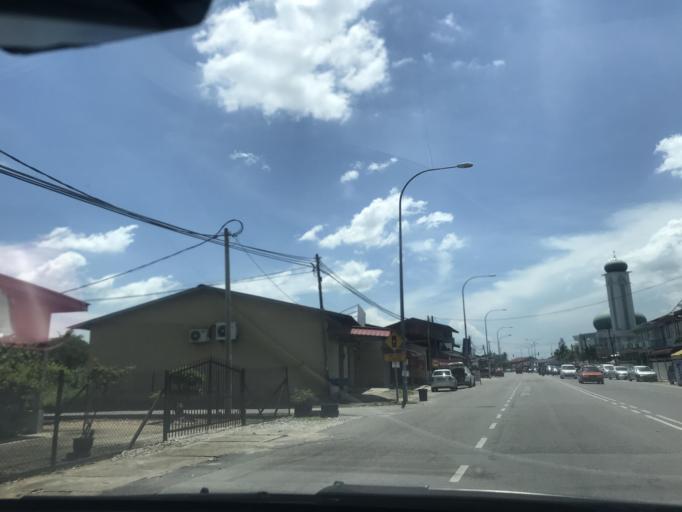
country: MY
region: Kelantan
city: Kota Bharu
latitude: 6.1139
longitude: 102.2664
